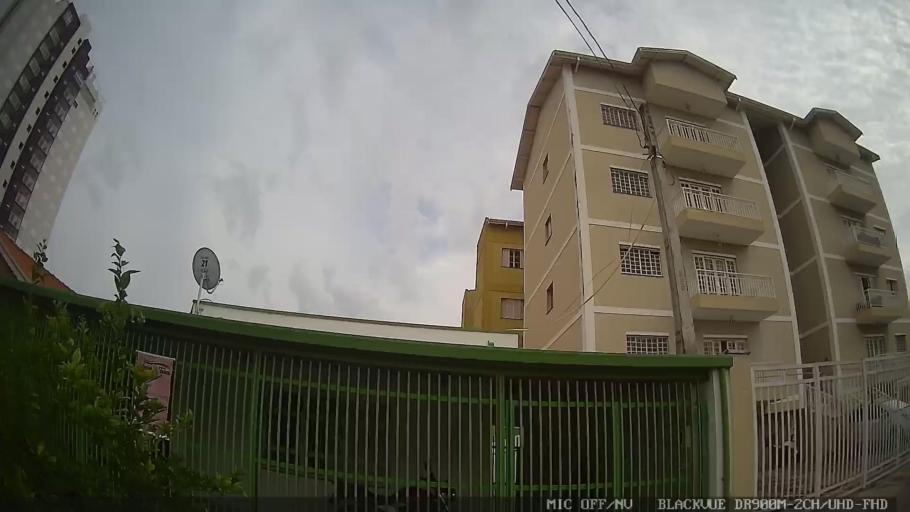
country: BR
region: Sao Paulo
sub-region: Indaiatuba
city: Indaiatuba
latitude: -23.0914
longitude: -47.2003
